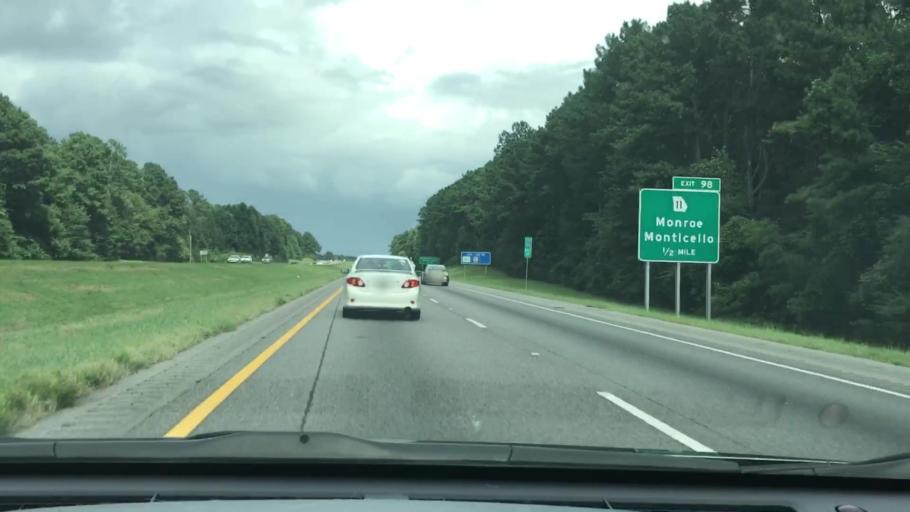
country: US
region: Georgia
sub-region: Walton County
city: Social Circle
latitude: 33.6114
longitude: -83.7638
